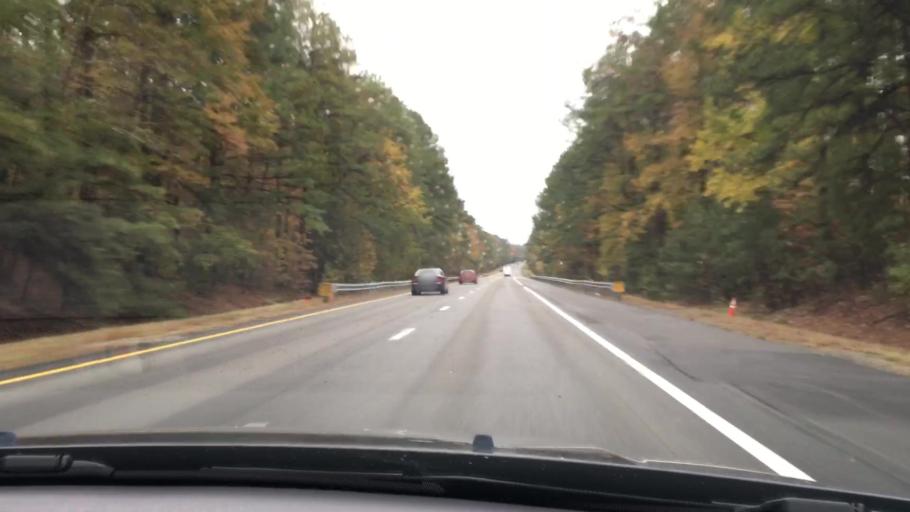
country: US
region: Virginia
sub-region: King William County
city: West Point
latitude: 37.4543
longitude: -76.8741
